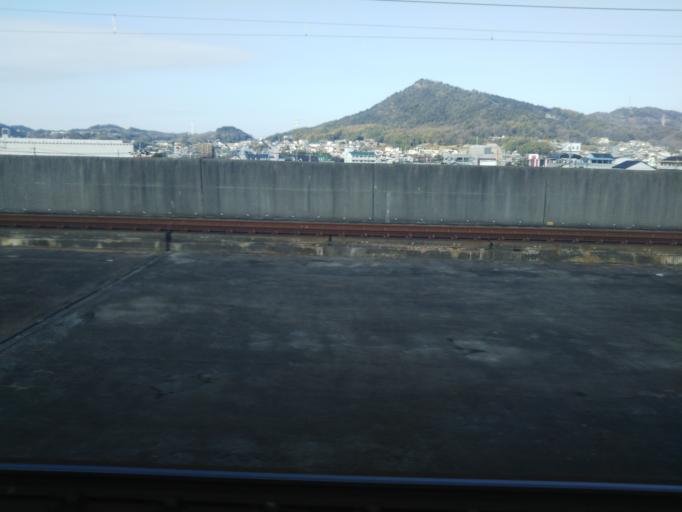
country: JP
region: Okayama
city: Kurashiki
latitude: 34.4606
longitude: 133.8073
